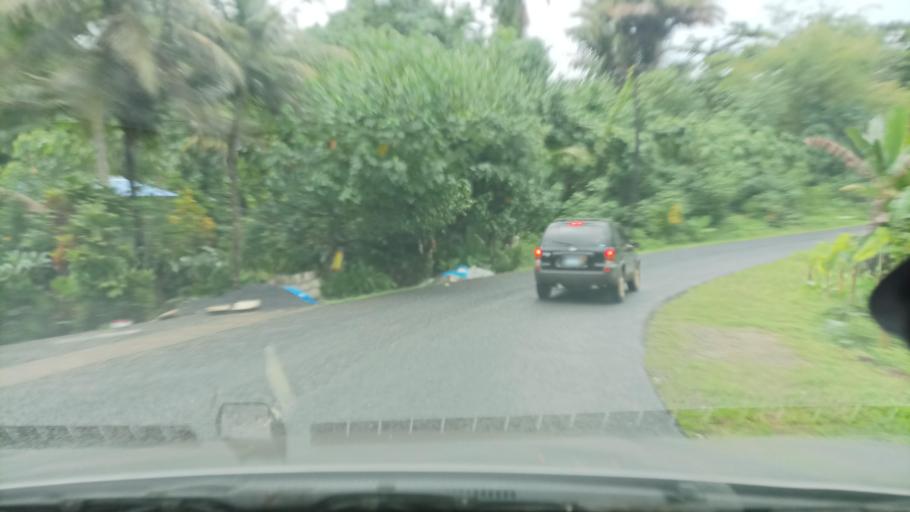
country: FM
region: Pohnpei
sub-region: Sokehs Municipality
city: Palikir - National Government Center
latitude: 6.8867
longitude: 158.1568
